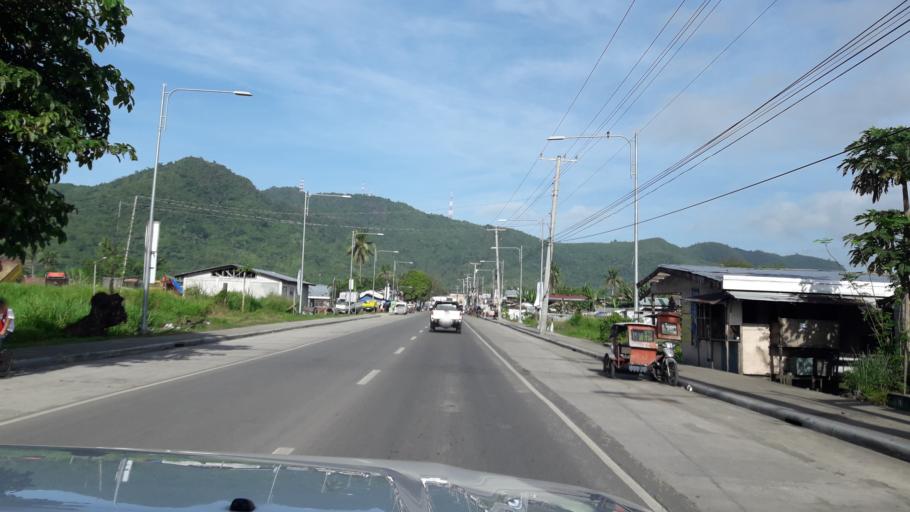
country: PH
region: Eastern Visayas
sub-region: Province of Leyte
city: Pawing
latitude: 11.2157
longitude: 124.9978
